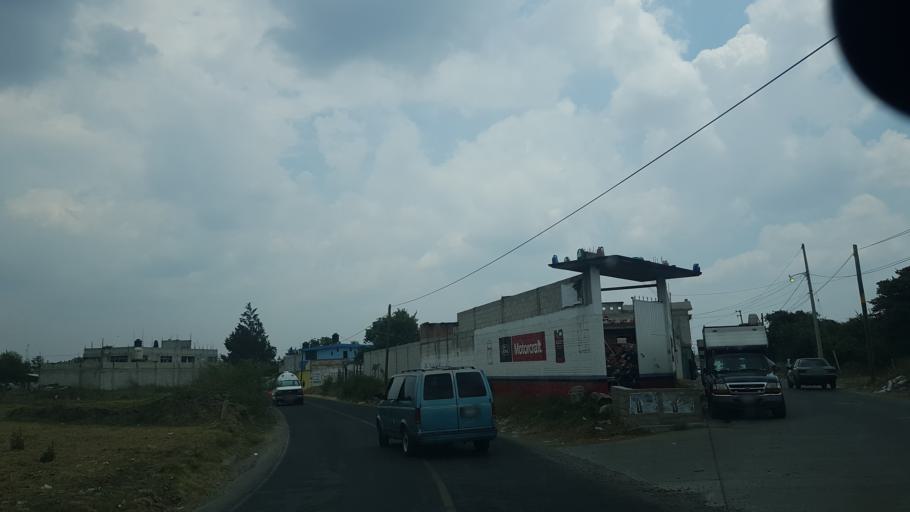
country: MX
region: Puebla
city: Huejotzingo
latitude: 19.1585
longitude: -98.4193
